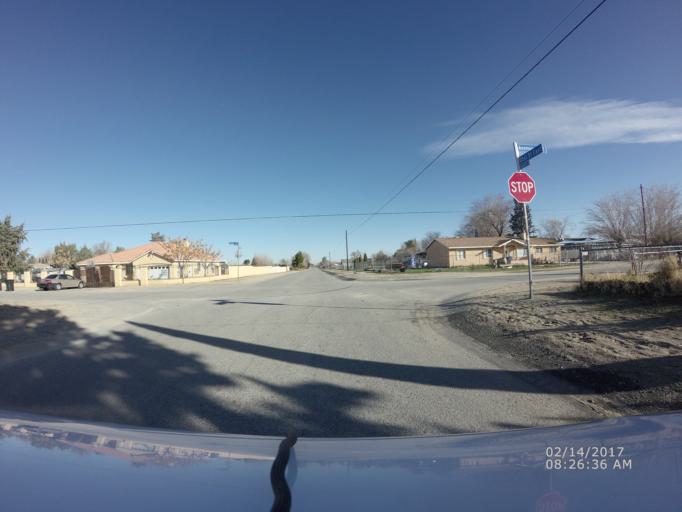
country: US
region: California
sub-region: Los Angeles County
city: Littlerock
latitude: 34.5465
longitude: -117.9494
